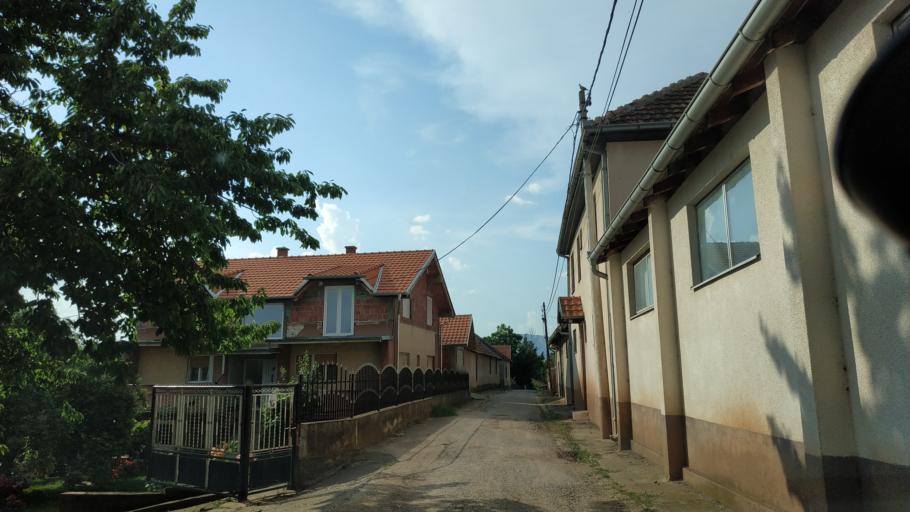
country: RS
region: Central Serbia
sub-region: Nisavski Okrug
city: Aleksinac
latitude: 43.6038
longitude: 21.6962
